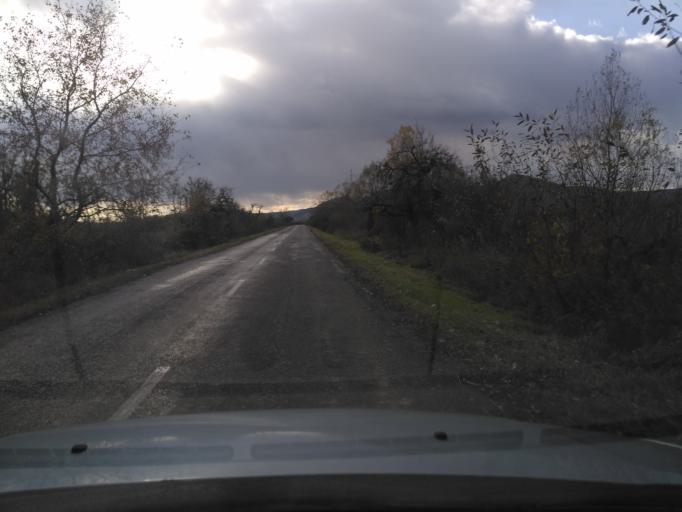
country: HU
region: Borsod-Abauj-Zemplen
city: Satoraljaujhely
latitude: 48.4148
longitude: 21.7205
